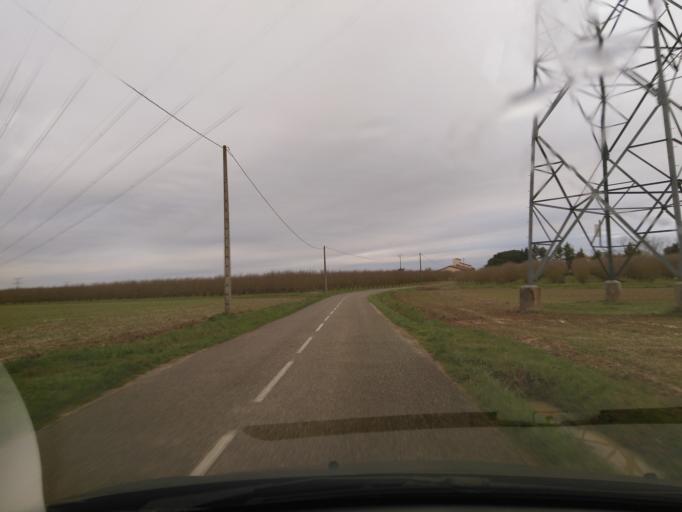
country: FR
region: Midi-Pyrenees
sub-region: Departement du Tarn-et-Garonne
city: Finhan
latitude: 43.8888
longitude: 1.1380
